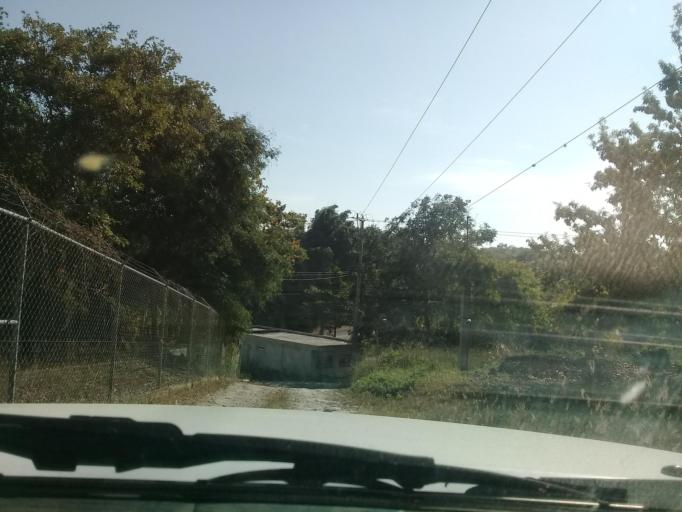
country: MX
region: Veracruz
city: Rinconada
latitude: 19.4012
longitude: -96.5605
